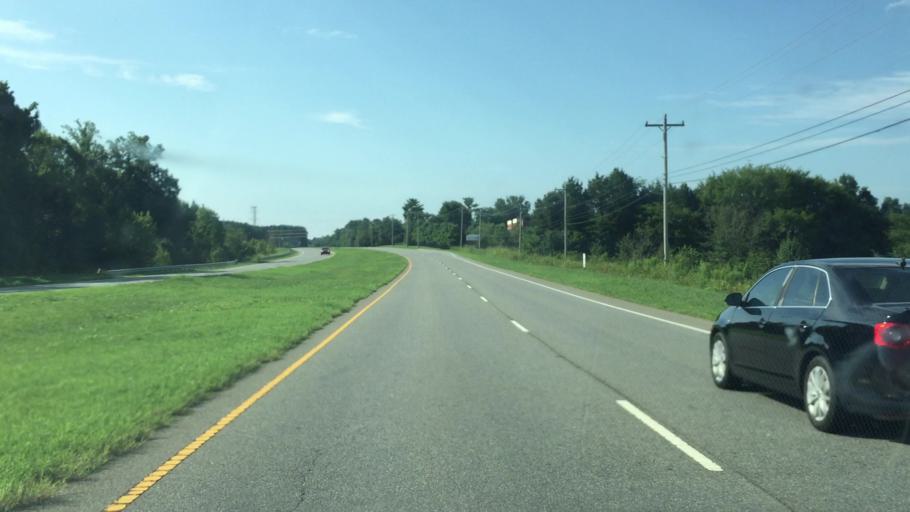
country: US
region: North Carolina
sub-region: Rowan County
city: Enochville
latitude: 35.4784
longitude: -80.6733
